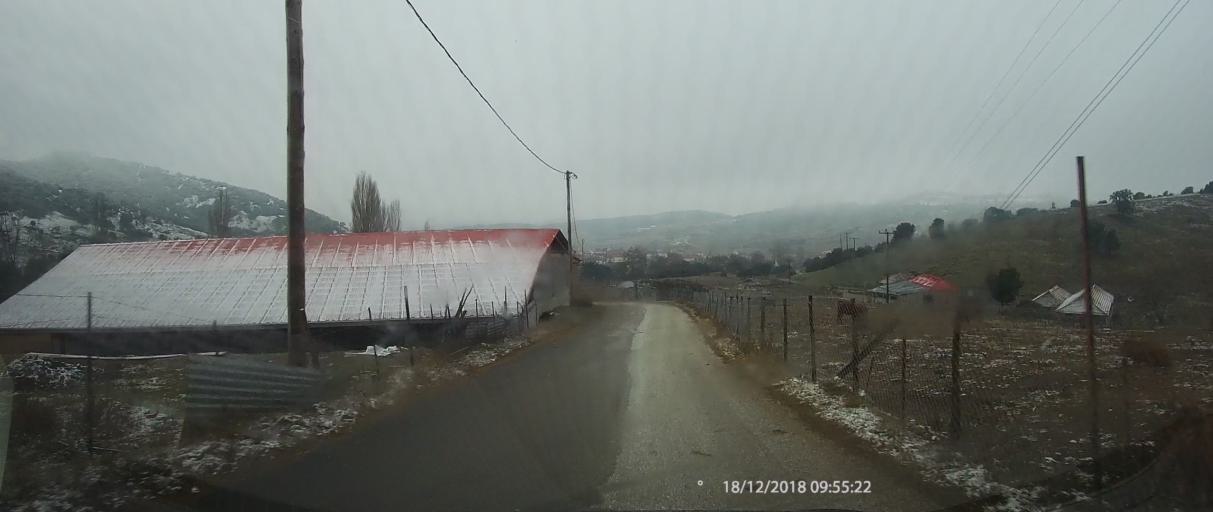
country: GR
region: Thessaly
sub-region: Nomos Larisis
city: Livadi
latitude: 40.0254
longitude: 22.2496
